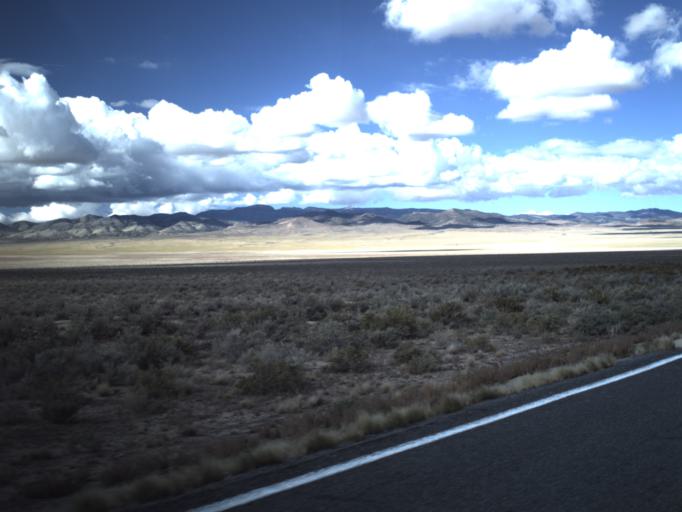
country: US
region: Utah
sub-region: Beaver County
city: Milford
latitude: 38.5465
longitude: -113.7202
